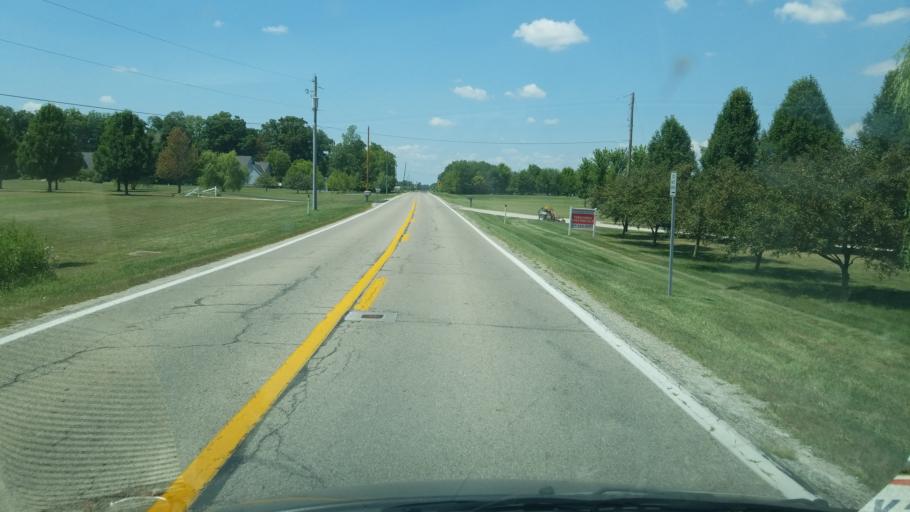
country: US
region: Ohio
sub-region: Franklin County
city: Lake Darby
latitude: 39.9821
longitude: -83.2255
